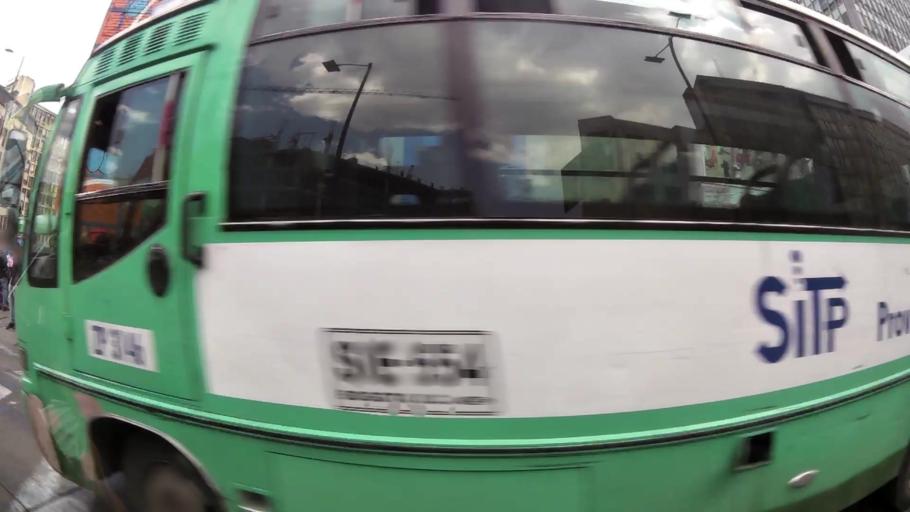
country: CO
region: Bogota D.C.
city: Bogota
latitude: 4.6026
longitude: -74.0766
